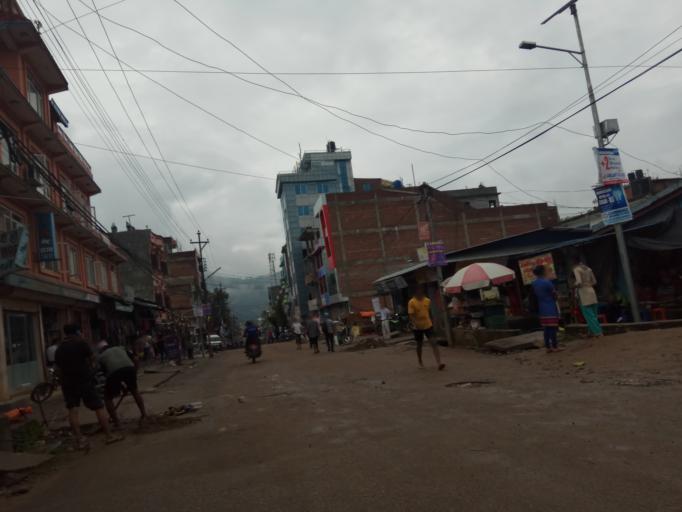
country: NP
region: Central Region
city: Kirtipur
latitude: 27.9110
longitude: 84.8940
